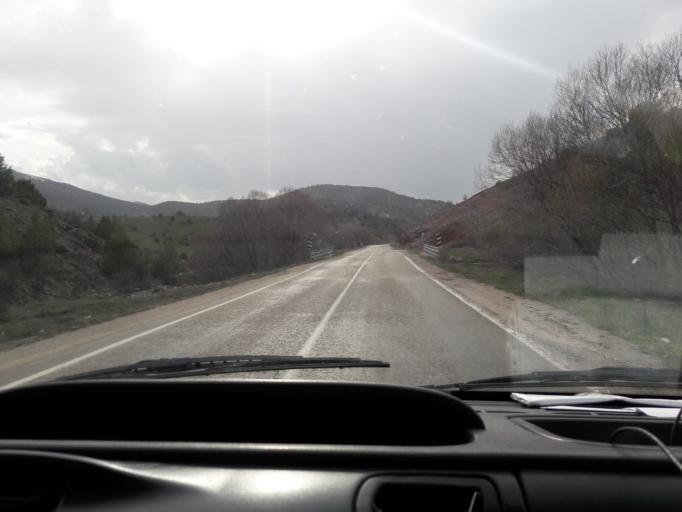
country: TR
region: Giresun
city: Alucra
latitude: 40.2646
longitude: 38.8977
